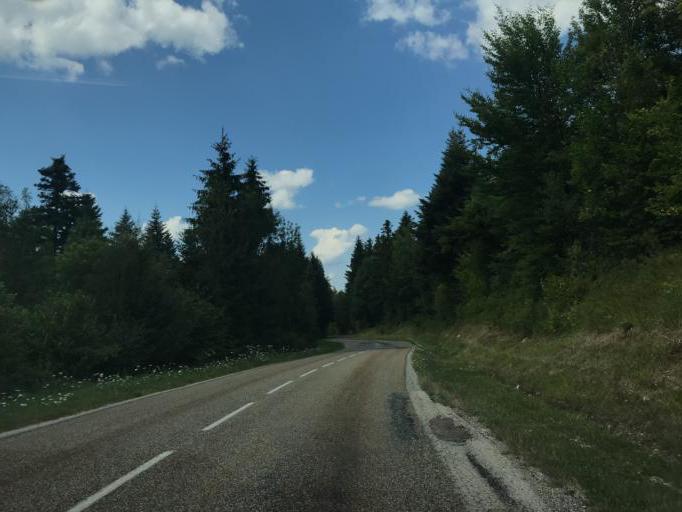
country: FR
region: Franche-Comte
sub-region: Departement du Jura
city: Clairvaux-les-Lacs
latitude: 46.5577
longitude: 5.7699
